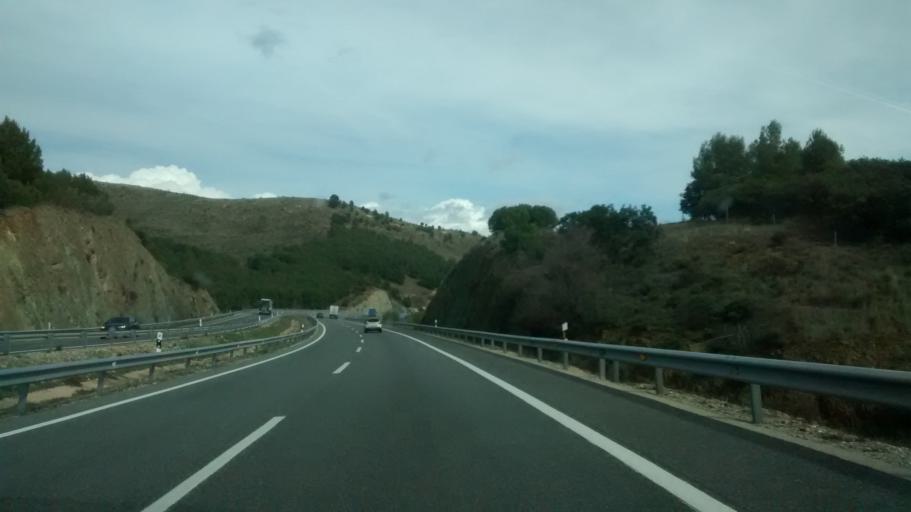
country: ES
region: Aragon
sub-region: Provincia de Zaragoza
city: Bubierca
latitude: 41.3201
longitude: -1.8449
